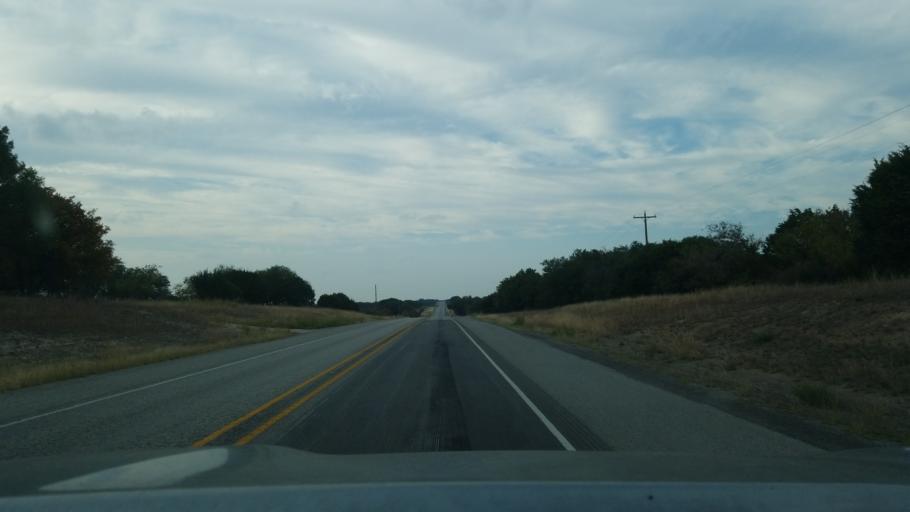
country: US
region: Texas
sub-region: Mills County
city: Goldthwaite
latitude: 31.5263
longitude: -98.6043
